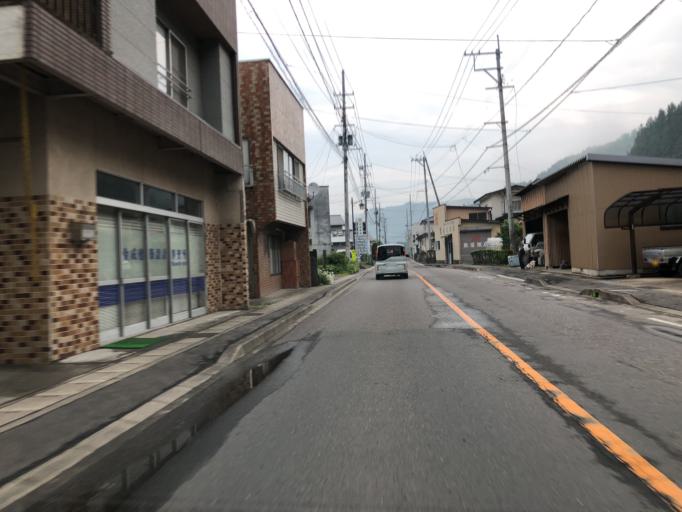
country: JP
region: Fukushima
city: Ishikawa
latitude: 37.1540
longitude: 140.4584
